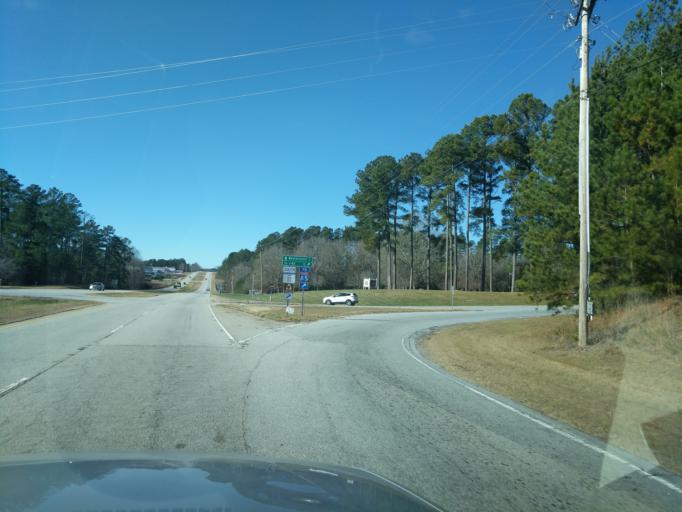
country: US
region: South Carolina
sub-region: Oconee County
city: Westminster
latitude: 34.6648
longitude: -83.0409
